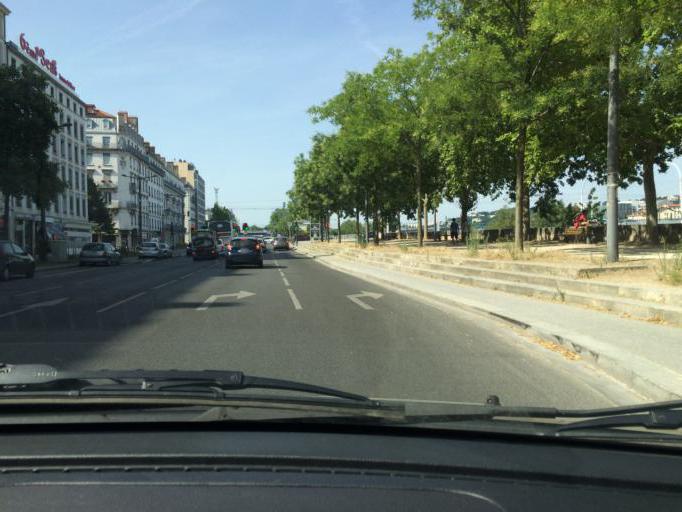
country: FR
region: Rhone-Alpes
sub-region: Departement du Rhone
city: Lyon
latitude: 45.7488
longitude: 4.8343
